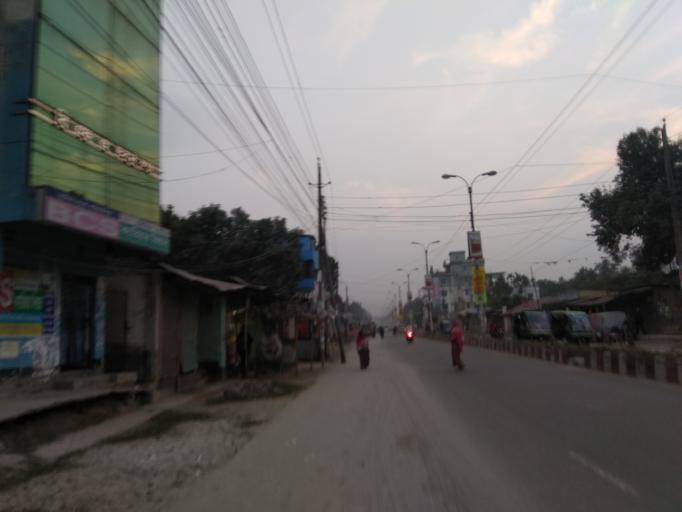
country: BD
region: Rangpur Division
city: Rangpur
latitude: 25.7320
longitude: 89.2548
